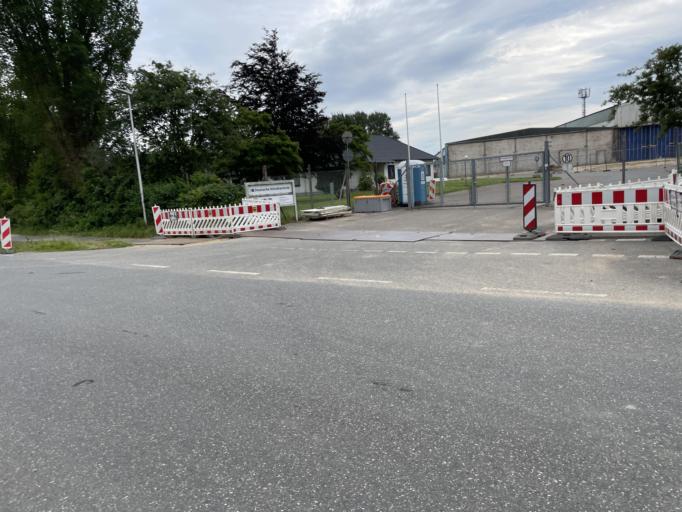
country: DE
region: Schleswig-Holstein
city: Mildstedt
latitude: 54.4680
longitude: 9.0907
